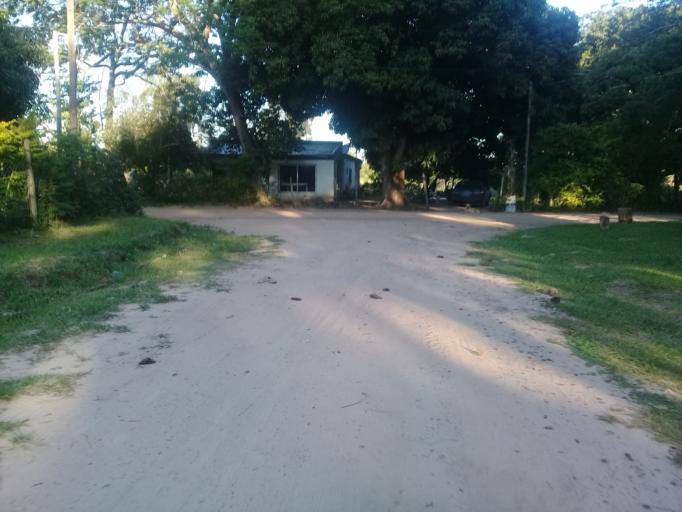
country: AR
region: Corrientes
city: San Luis del Palmar
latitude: -27.4655
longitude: -58.6627
